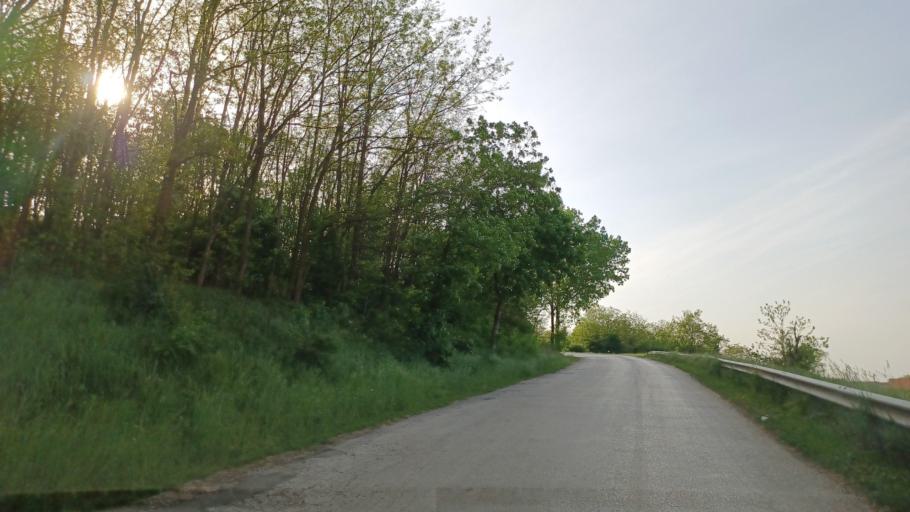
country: HU
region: Baranya
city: Villany
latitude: 45.9545
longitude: 18.3872
